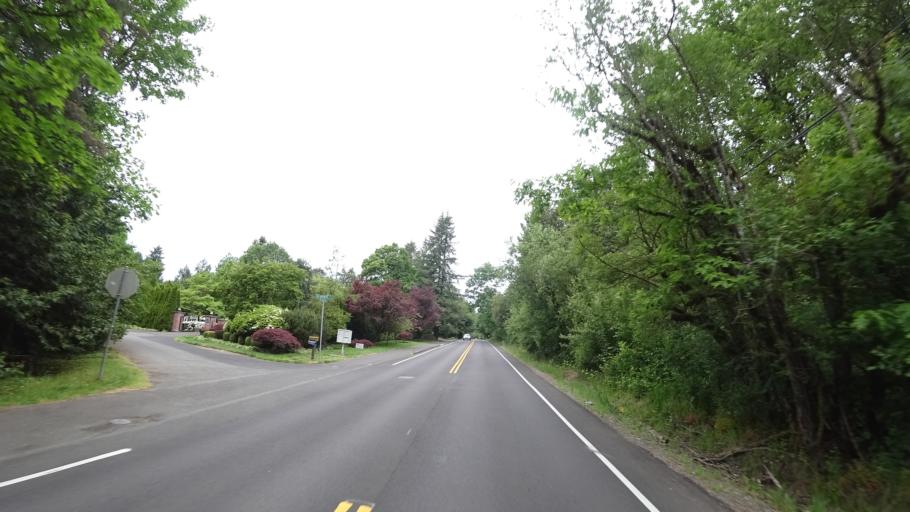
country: US
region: Oregon
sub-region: Clackamas County
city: Lake Oswego
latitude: 45.4356
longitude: -122.6675
